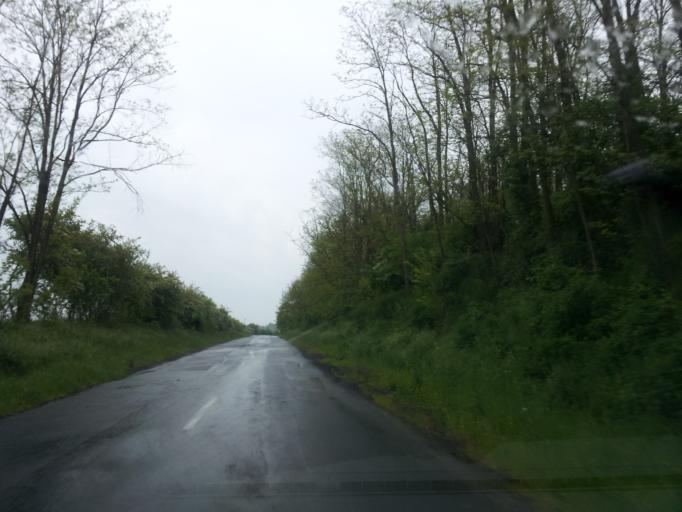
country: HU
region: Tolna
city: Szekszard
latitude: 46.2878
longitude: 18.6625
